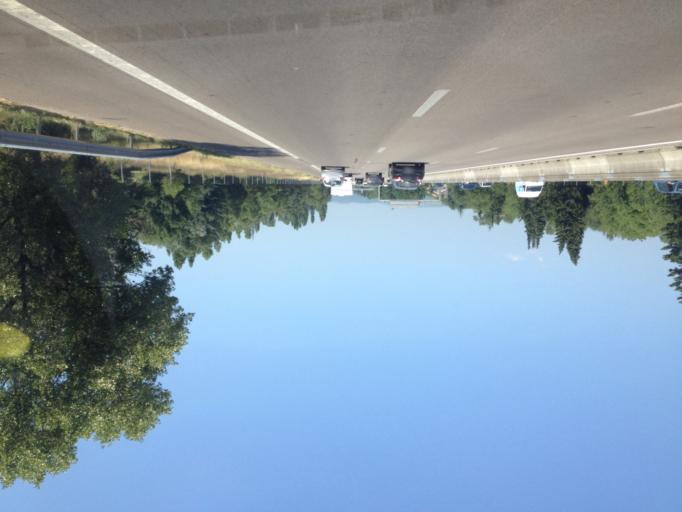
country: FR
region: Rhone-Alpes
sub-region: Departement de la Drome
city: Saulce-sur-Rhone
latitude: 44.7003
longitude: 4.7875
